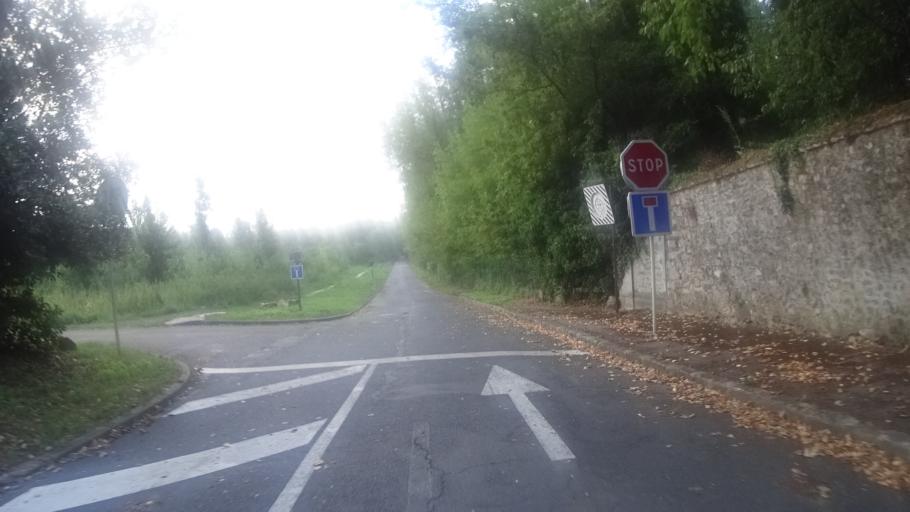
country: FR
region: Ile-de-France
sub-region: Departement de l'Essonne
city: Mennecy
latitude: 48.5696
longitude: 2.4124
